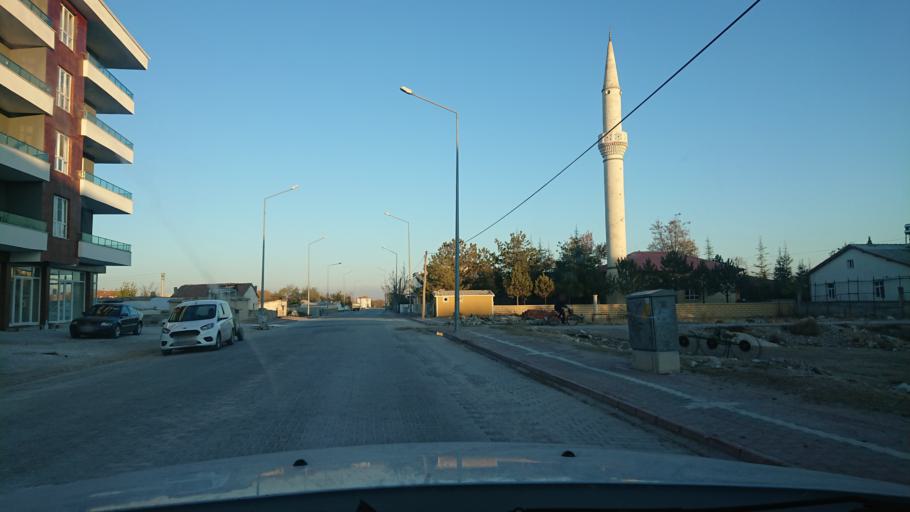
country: TR
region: Aksaray
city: Eskil
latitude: 38.4019
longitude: 33.4163
